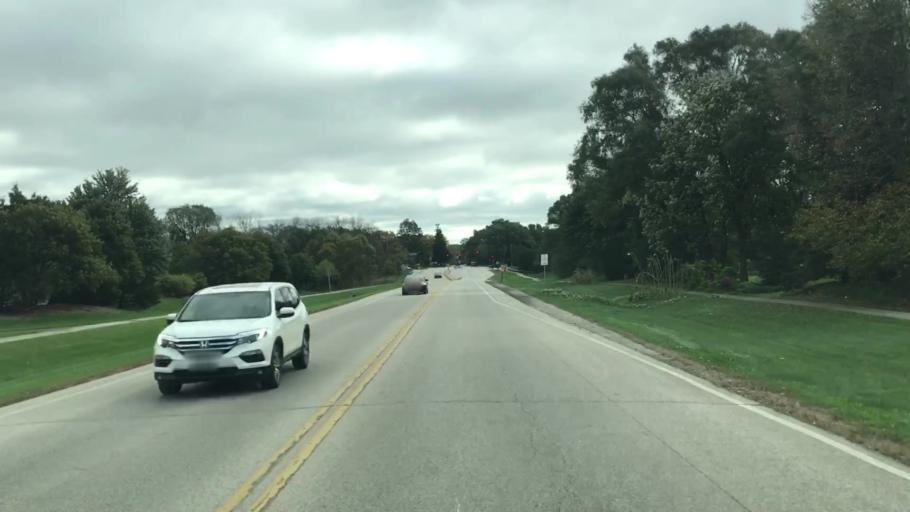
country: US
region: Wisconsin
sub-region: Waukesha County
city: Brookfield
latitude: 43.0606
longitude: -88.1130
